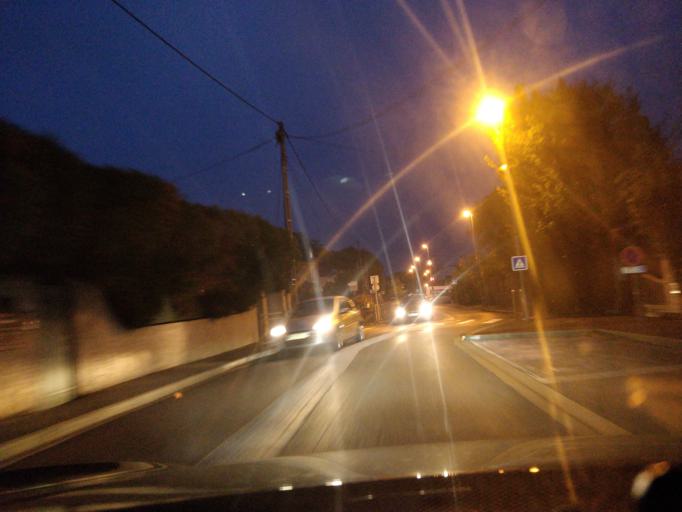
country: FR
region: Ile-de-France
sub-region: Departement de l'Essonne
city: Forges-les-Bains
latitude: 48.6296
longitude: 2.0882
